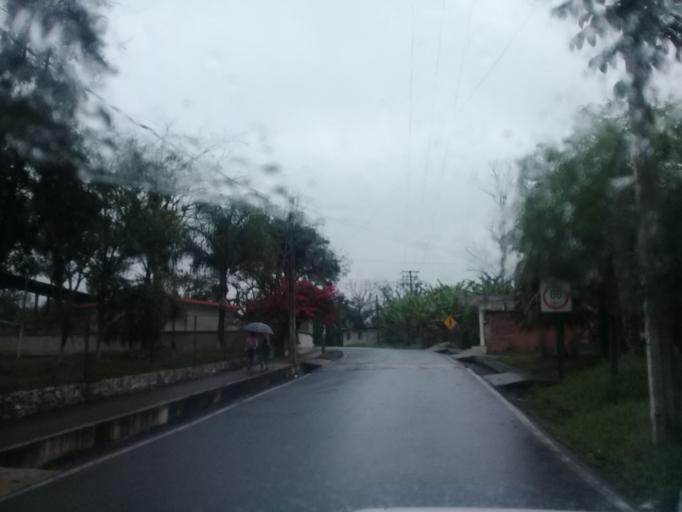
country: MX
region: Veracruz
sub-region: Amatlan de los Reyes
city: Centro de Readaptacion Social
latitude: 18.8027
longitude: -96.9513
